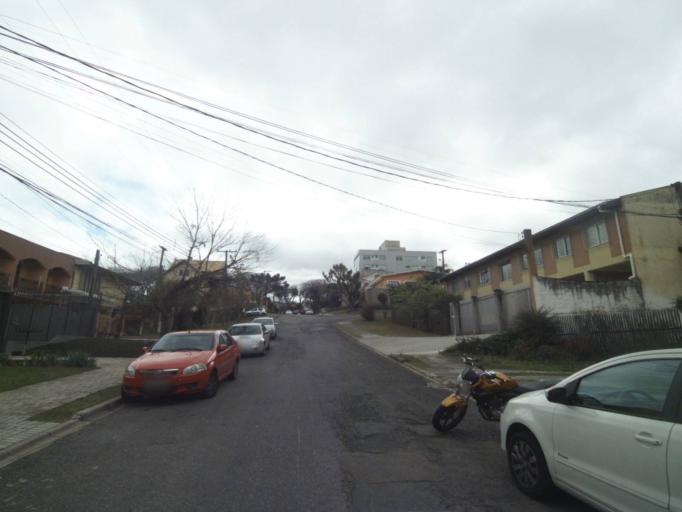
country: BR
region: Parana
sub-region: Curitiba
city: Curitiba
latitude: -25.4565
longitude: -49.2983
